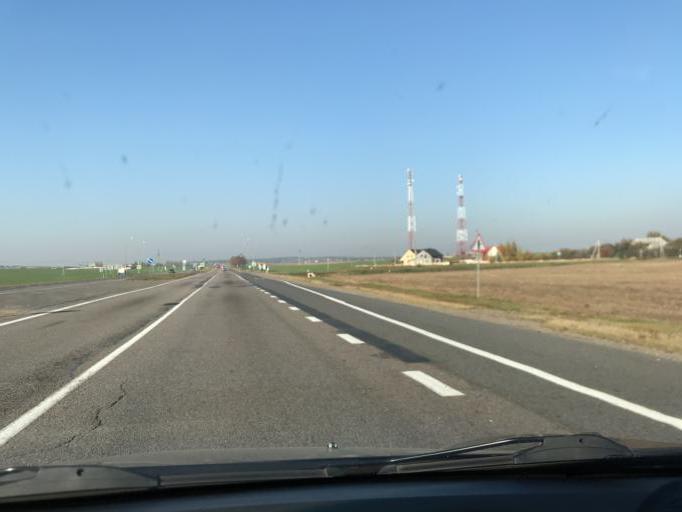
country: BY
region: Minsk
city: Luhavaya Slabada
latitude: 53.7336
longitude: 27.8501
